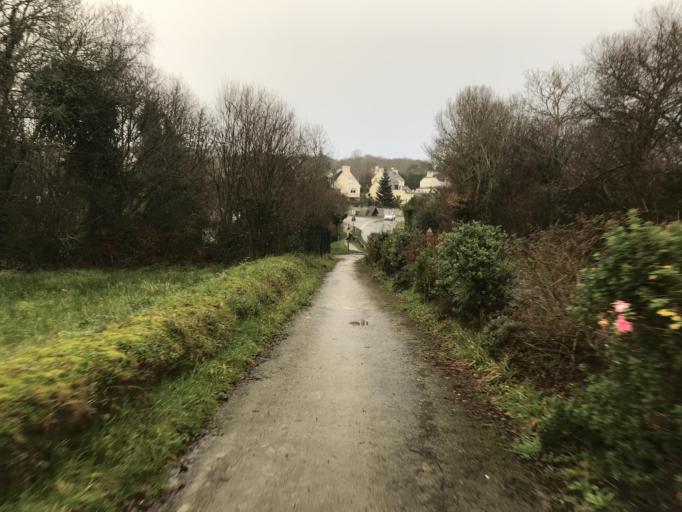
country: FR
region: Brittany
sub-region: Departement du Finistere
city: Loperhet
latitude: 48.3648
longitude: -4.3095
